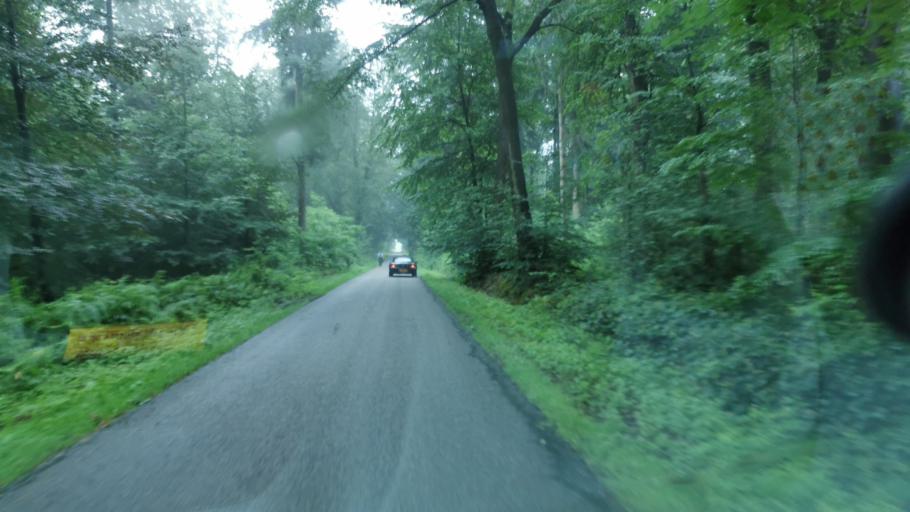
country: NL
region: Overijssel
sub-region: Gemeente Enschede
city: Enschede
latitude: 52.2421
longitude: 6.9367
